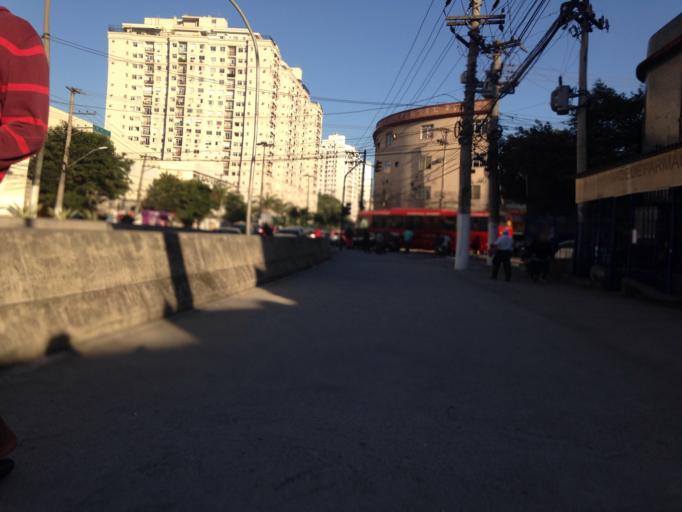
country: BR
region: Rio de Janeiro
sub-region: Niteroi
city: Niteroi
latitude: -22.8951
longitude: -43.1130
